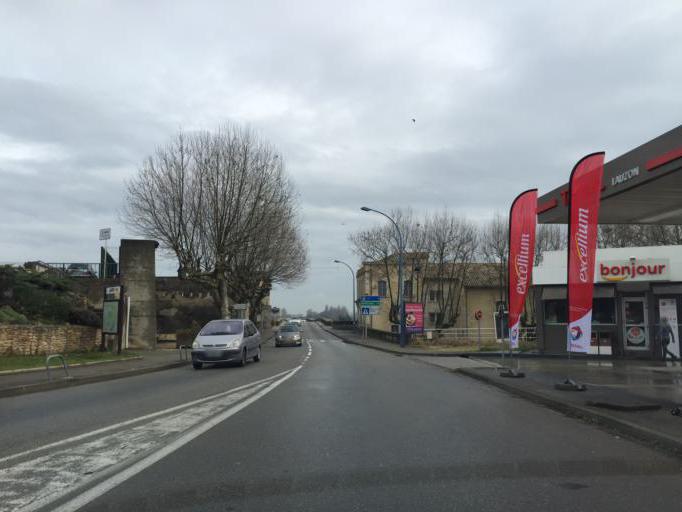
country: FR
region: Languedoc-Roussillon
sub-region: Departement du Gard
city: Pont-Saint-Esprit
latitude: 44.2585
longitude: 4.6492
